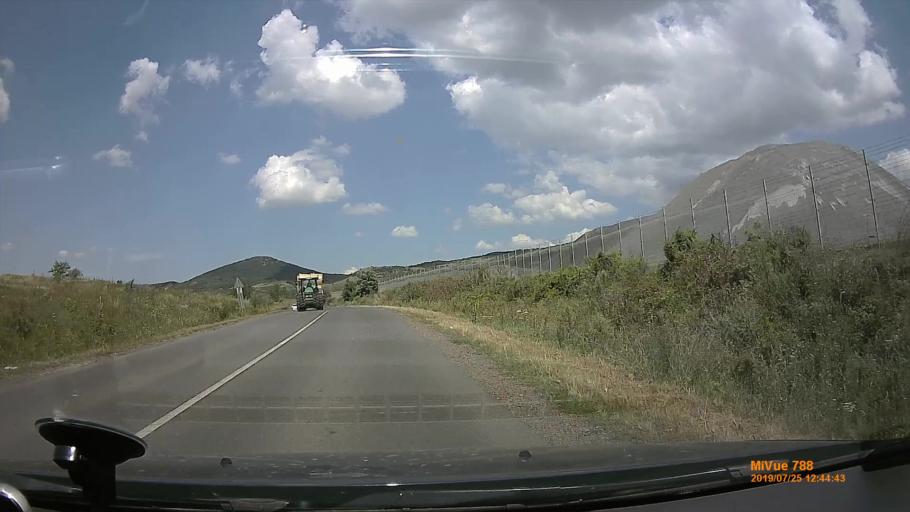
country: HU
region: Borsod-Abauj-Zemplen
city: Tallya
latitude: 48.2370
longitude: 21.2127
